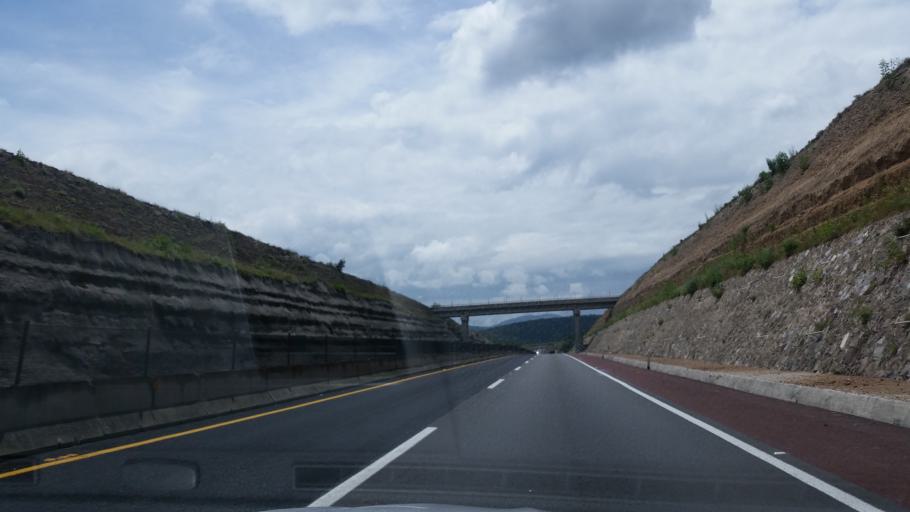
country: MX
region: Hidalgo
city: Tula de Allende
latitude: 20.0663
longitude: -99.3799
